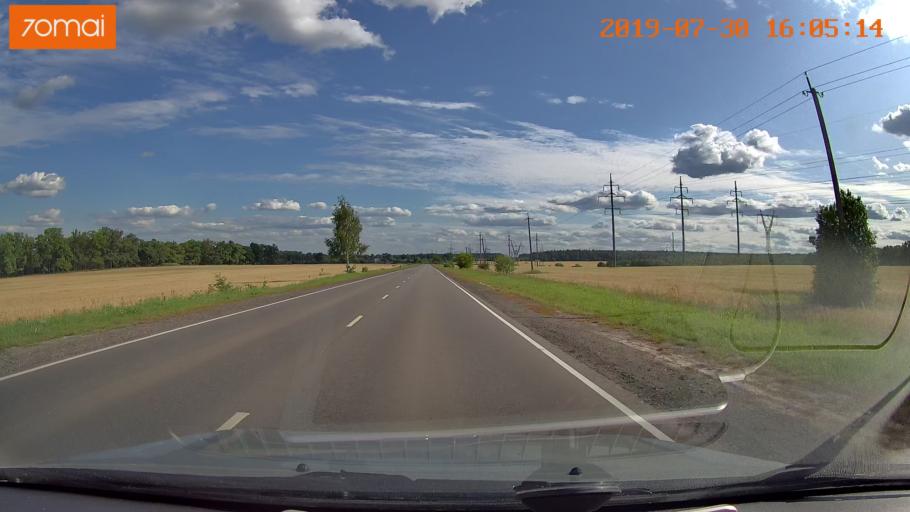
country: RU
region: Moskovskaya
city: Peski
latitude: 55.2688
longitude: 38.7143
